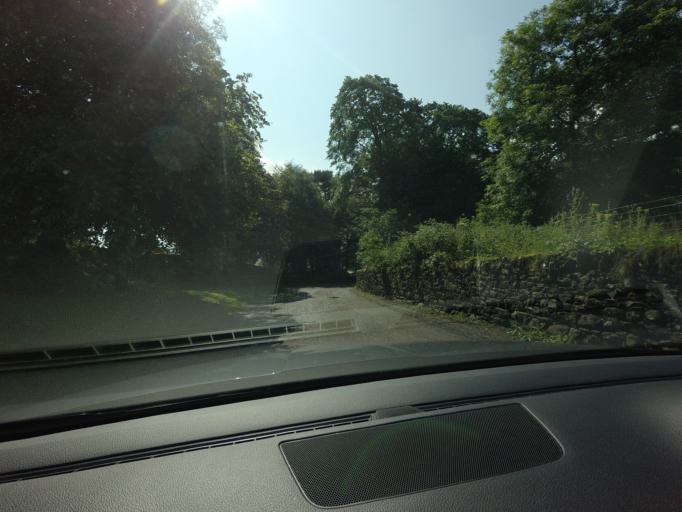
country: GB
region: Scotland
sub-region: Highland
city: Alness
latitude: 57.6894
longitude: -4.2406
